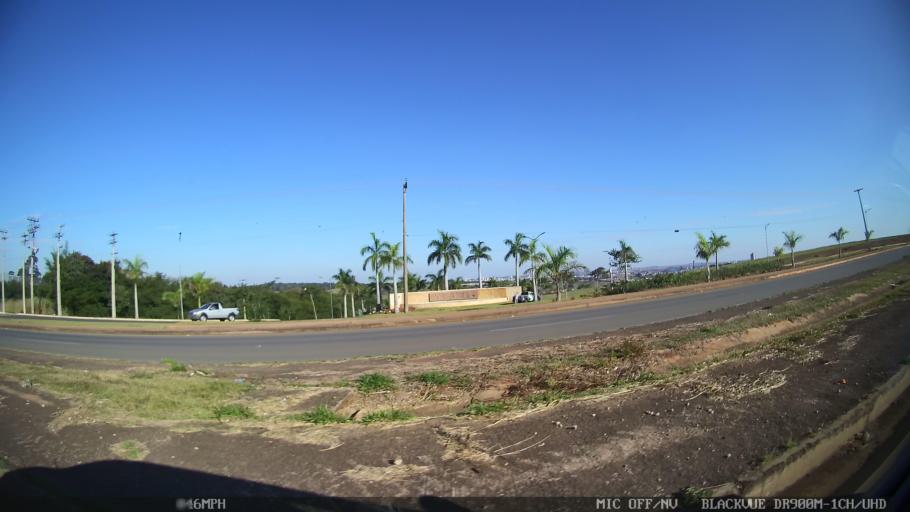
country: BR
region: Sao Paulo
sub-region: Nova Odessa
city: Nova Odessa
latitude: -22.7666
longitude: -47.2653
